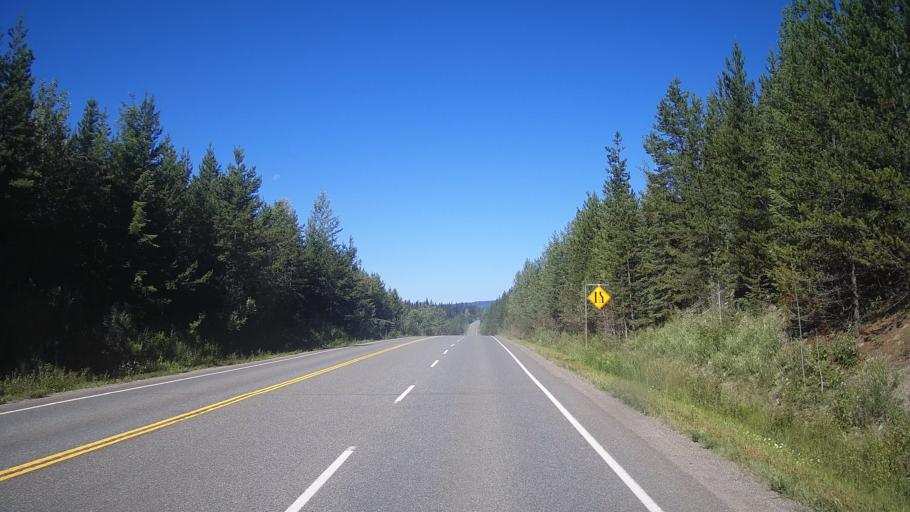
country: CA
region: British Columbia
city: Kamloops
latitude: 51.4973
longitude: -120.3765
